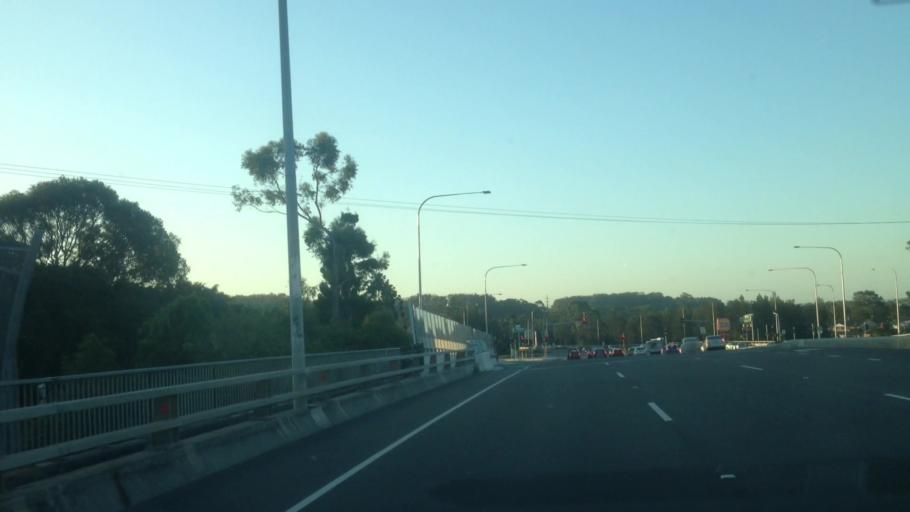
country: AU
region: New South Wales
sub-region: Wyong Shire
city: Chittaway Bay
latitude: -33.3104
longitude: 151.4196
